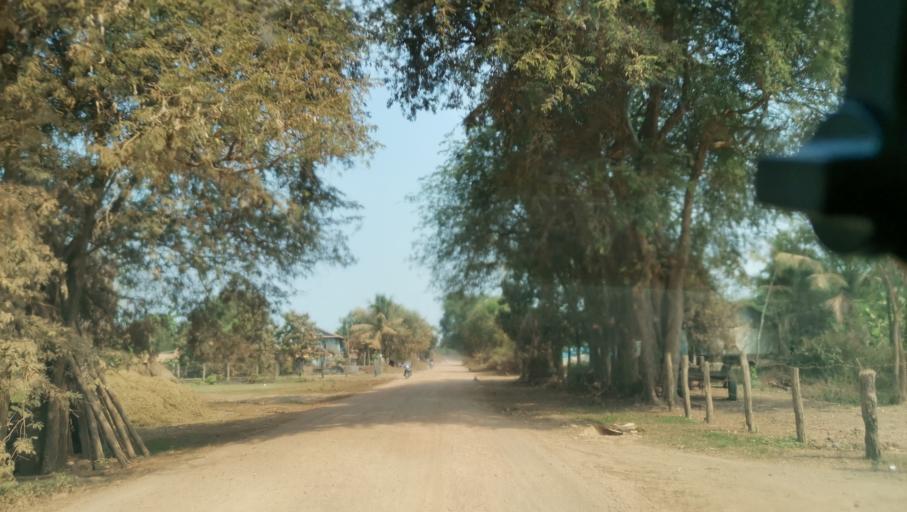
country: KH
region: Battambang
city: Battambang
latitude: 13.0635
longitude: 103.1684
